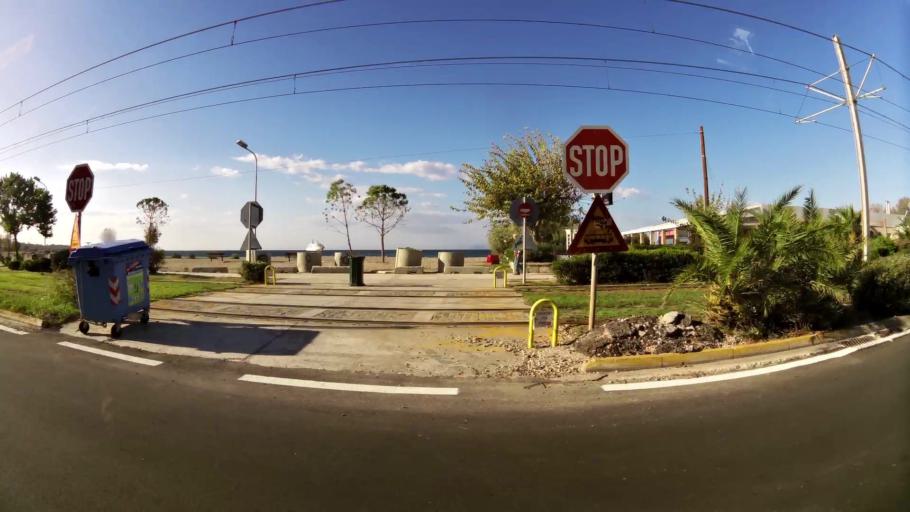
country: GR
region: Attica
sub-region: Nomarchia Athinas
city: Glyfada
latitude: 37.8662
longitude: 23.7407
